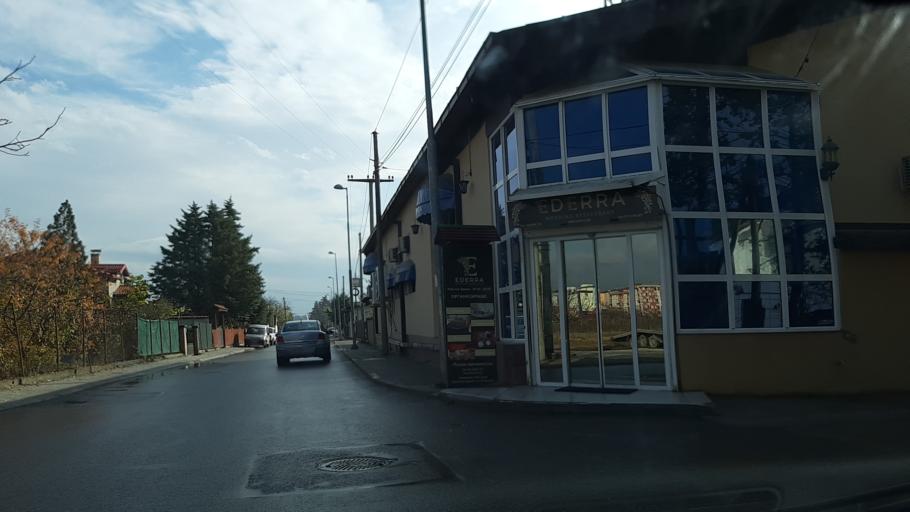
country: MK
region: Kisela Voda
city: Usje
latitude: 41.9786
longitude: 21.4819
